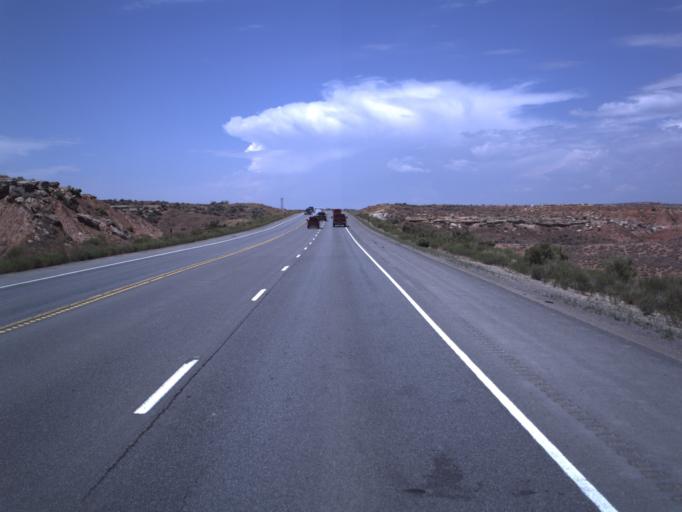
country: US
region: Utah
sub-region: Uintah County
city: Maeser
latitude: 40.3147
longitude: -109.7222
